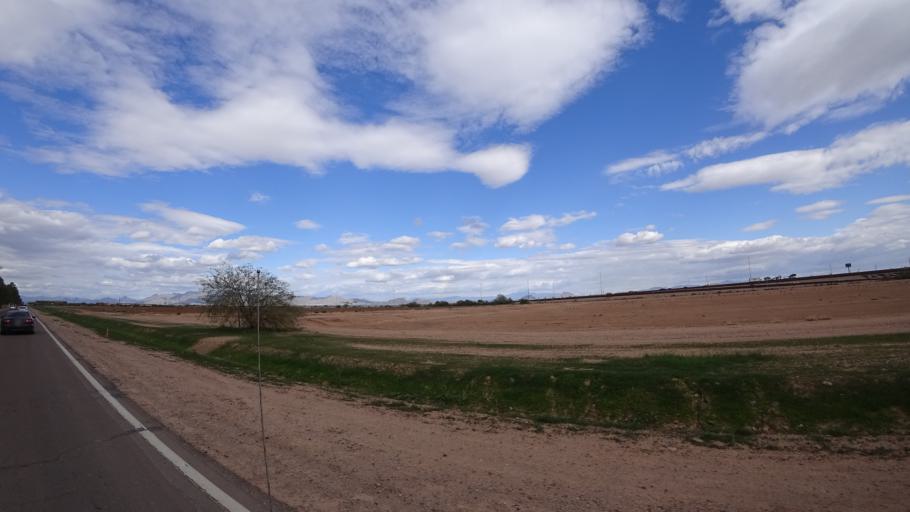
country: US
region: Arizona
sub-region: Maricopa County
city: Scottsdale
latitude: 33.4972
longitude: -111.8917
